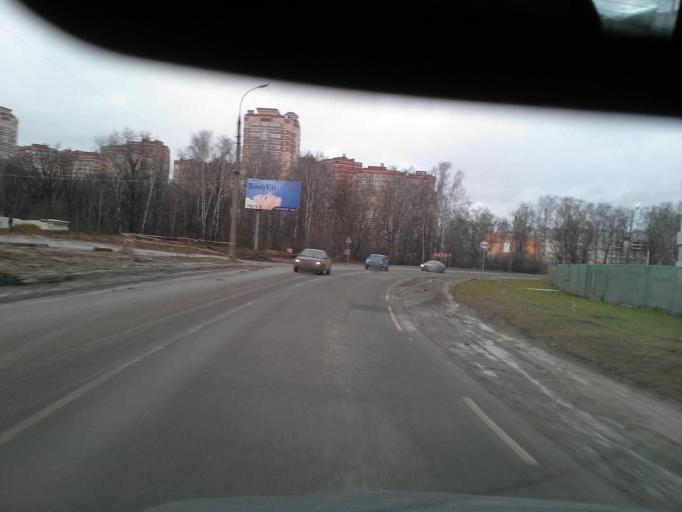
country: RU
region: Moskovskaya
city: Moskovskiy
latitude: 55.5911
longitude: 37.3473
